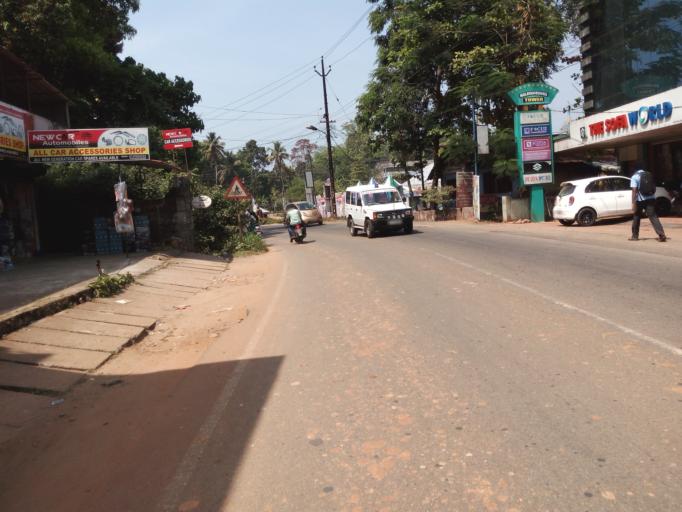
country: IN
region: Kerala
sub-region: Ernakulam
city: Muvattupula
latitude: 9.9067
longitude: 76.7101
